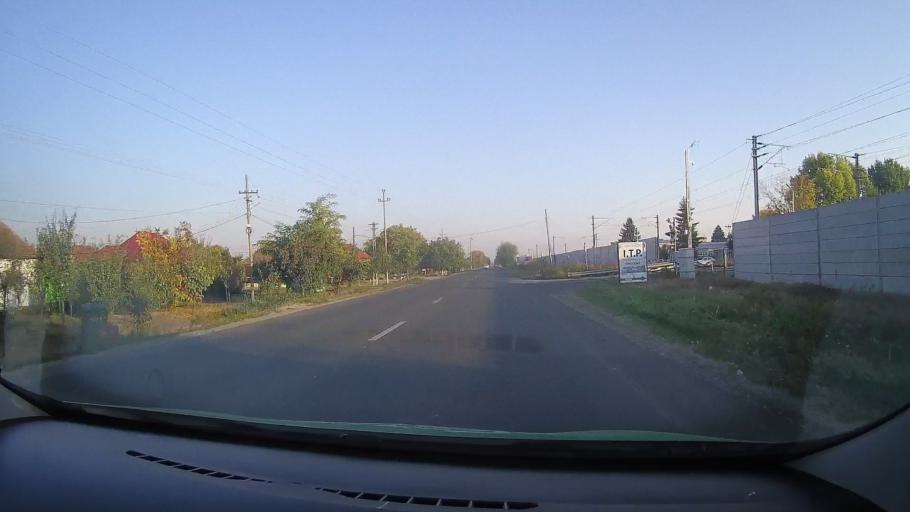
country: RO
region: Arad
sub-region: Comuna Sofronea
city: Sofronea
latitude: 46.2842
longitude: 21.3131
